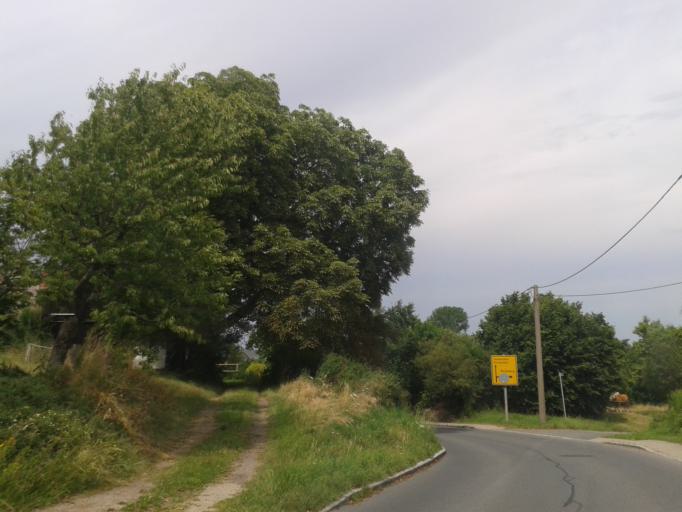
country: DE
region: Saxony
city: Reinsberg
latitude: 51.0077
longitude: 13.3384
